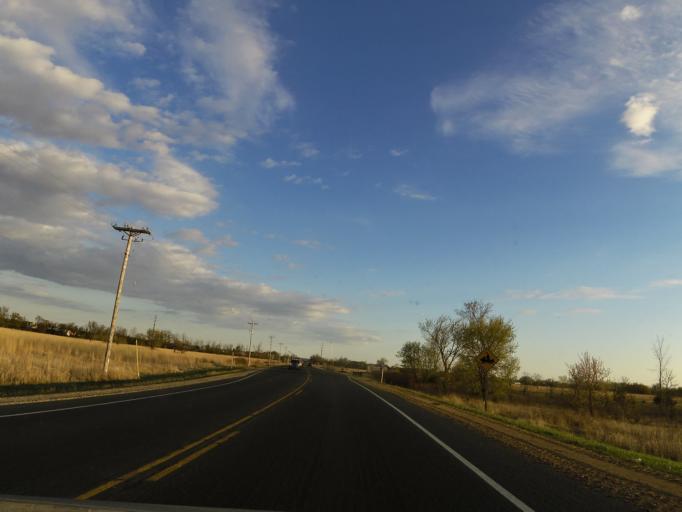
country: US
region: Wisconsin
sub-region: Saint Croix County
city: North Hudson
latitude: 45.0141
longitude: -92.6755
